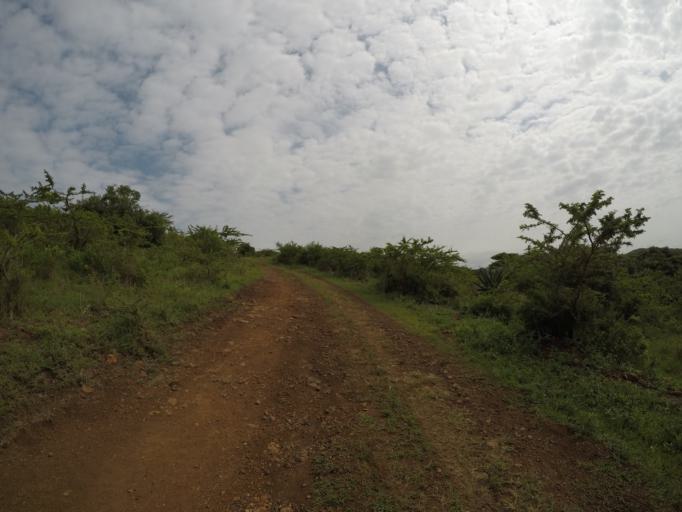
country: ZA
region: KwaZulu-Natal
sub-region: uThungulu District Municipality
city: Empangeni
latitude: -28.6227
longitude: 31.9107
